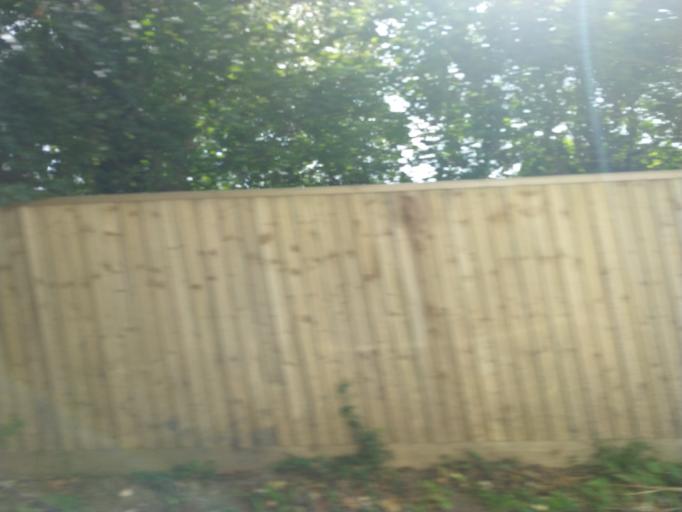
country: GB
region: England
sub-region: Dorset
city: Blandford Forum
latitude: 50.8536
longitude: -2.1501
